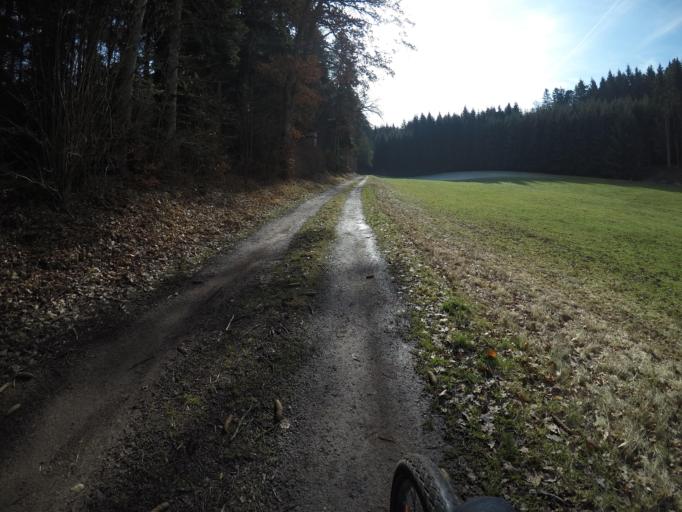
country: DE
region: Baden-Wuerttemberg
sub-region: Regierungsbezirk Stuttgart
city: Oberjettingen
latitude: 48.5986
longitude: 8.7902
